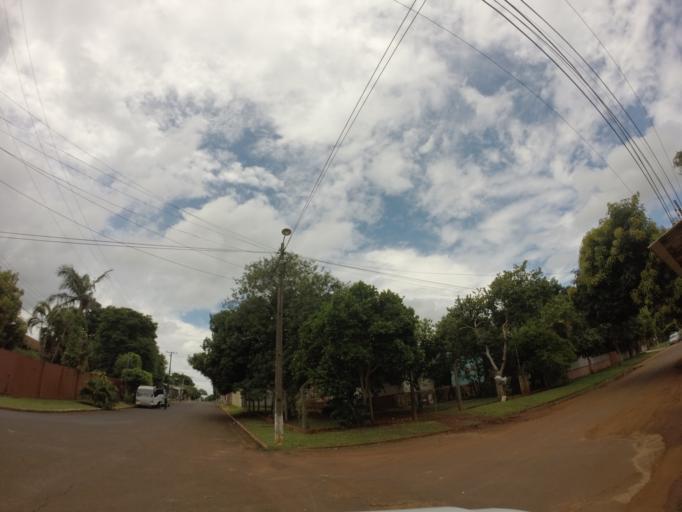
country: PY
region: Alto Parana
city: Ciudad del Este
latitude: -25.4170
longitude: -54.6287
